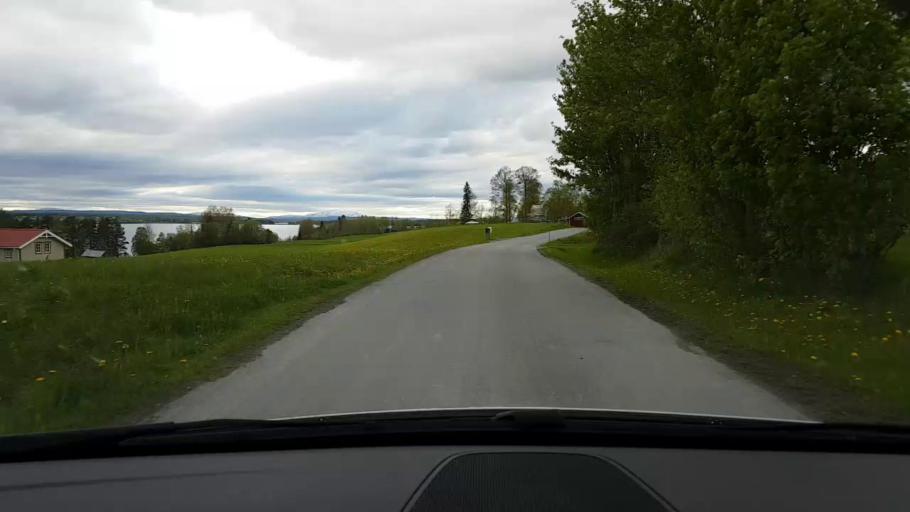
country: SE
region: Jaemtland
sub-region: Krokoms Kommun
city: Krokom
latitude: 63.2383
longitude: 14.0682
